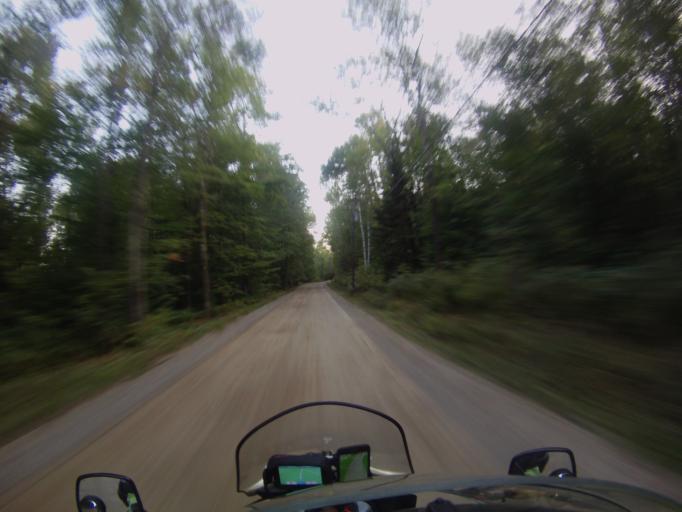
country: US
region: Vermont
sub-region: Addison County
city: Middlebury (village)
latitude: 44.0012
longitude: -73.0387
